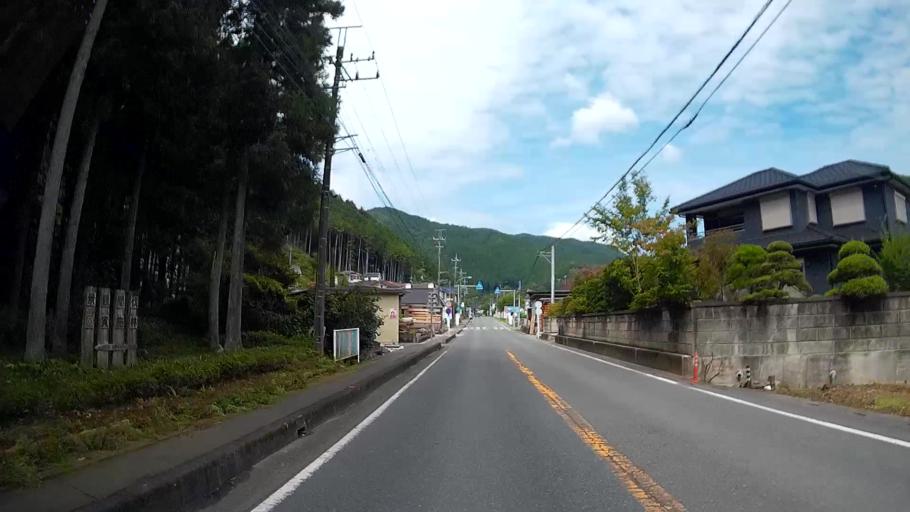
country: JP
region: Saitama
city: Hanno
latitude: 35.8707
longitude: 139.2402
